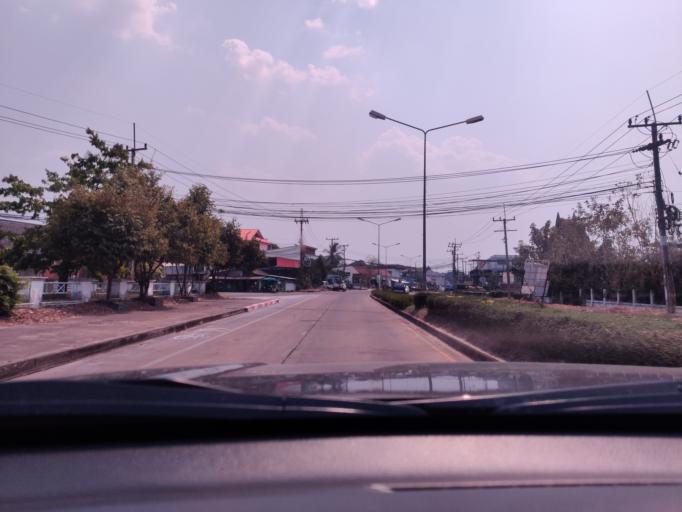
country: TH
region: Sisaket
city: Si Sa Ket
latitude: 15.1012
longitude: 104.3147
